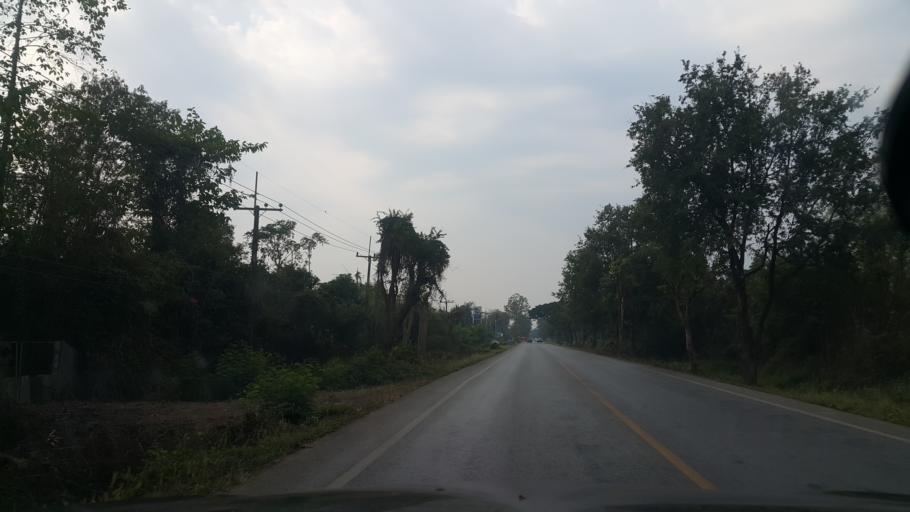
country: TH
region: Sukhothai
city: Si Samrong
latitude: 17.1056
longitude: 99.8884
